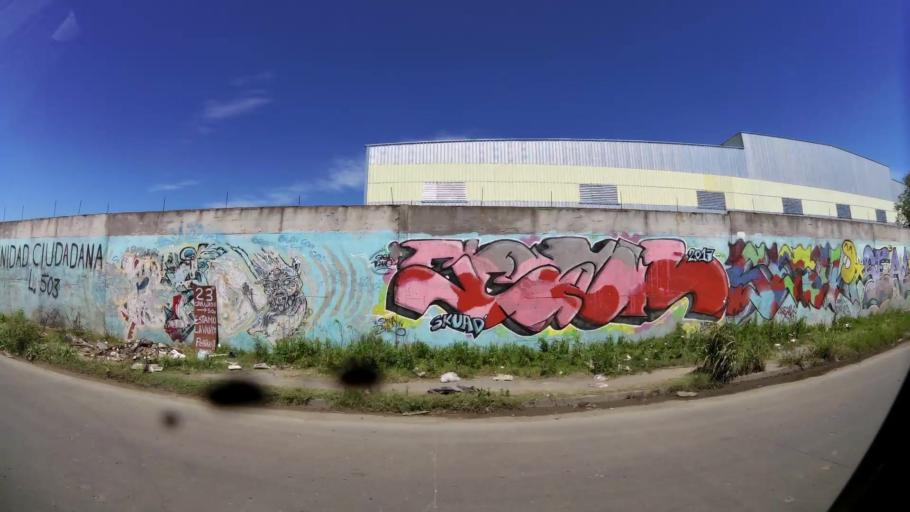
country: AR
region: Buenos Aires
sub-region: Partido de Lanus
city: Lanus
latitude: -34.7339
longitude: -58.3411
